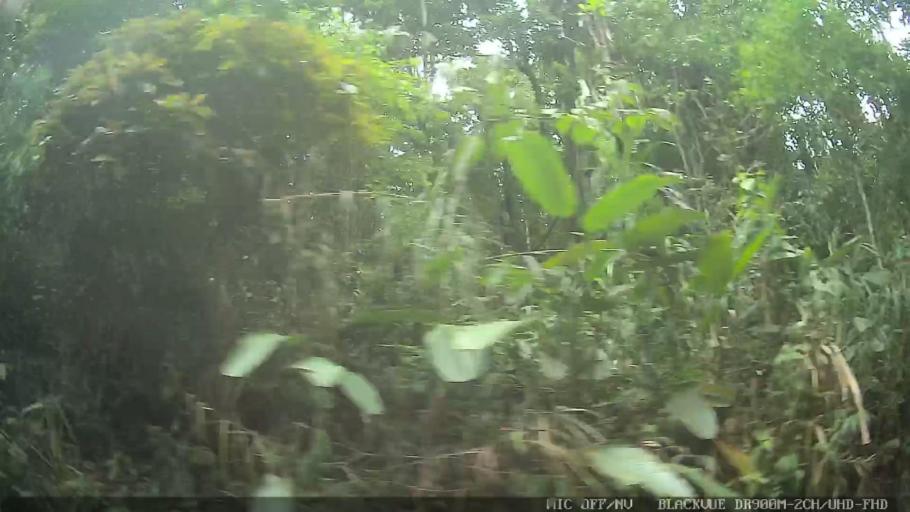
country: BR
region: Sao Paulo
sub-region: Mogi das Cruzes
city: Mogi das Cruzes
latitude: -23.4848
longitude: -46.2033
